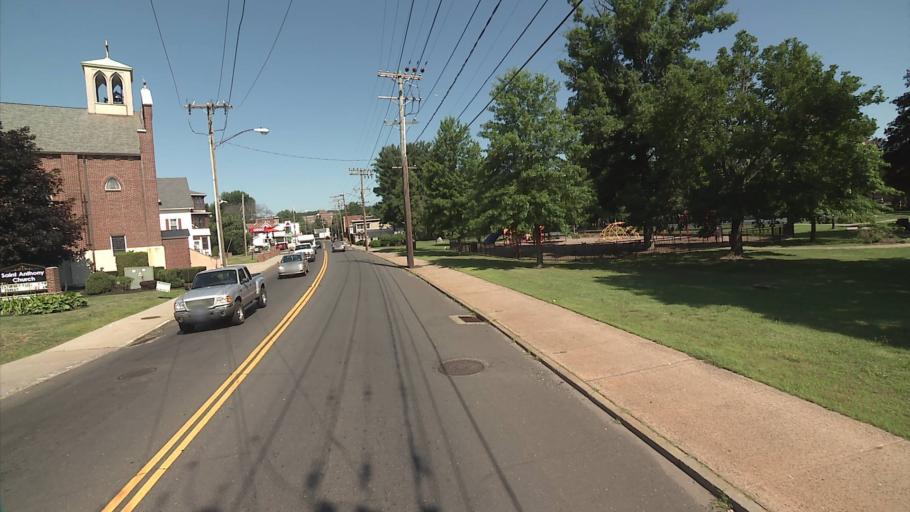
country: US
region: Connecticut
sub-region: Hartford County
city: Bristol
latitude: 41.6709
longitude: -72.9463
